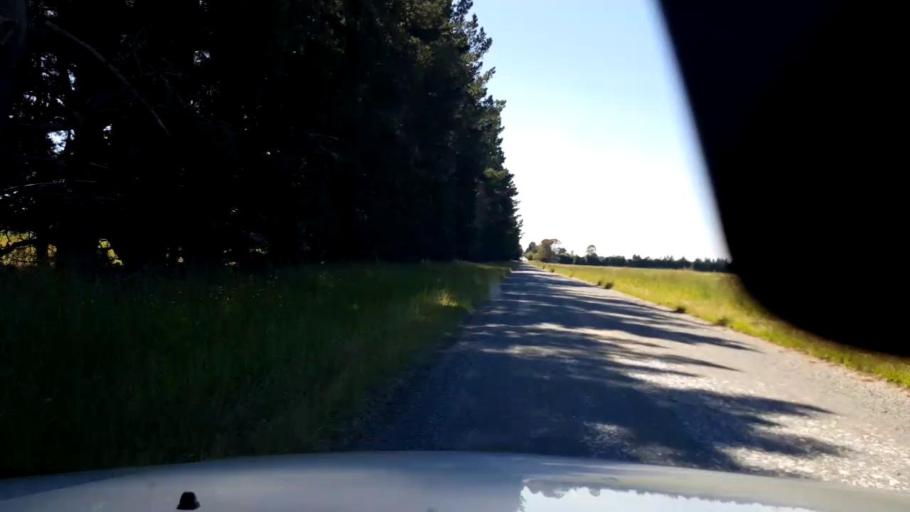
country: NZ
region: Canterbury
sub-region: Timaru District
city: Pleasant Point
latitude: -43.9738
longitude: 171.2544
